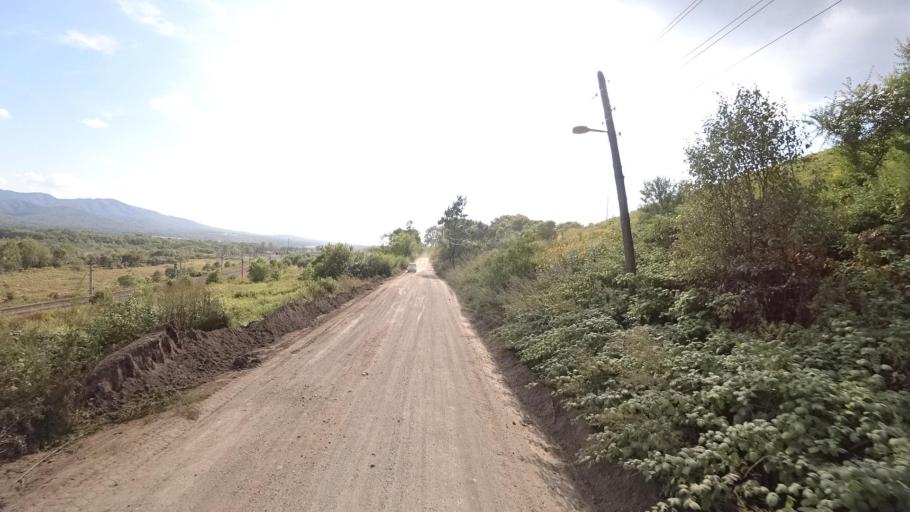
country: RU
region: Jewish Autonomous Oblast
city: Birakan
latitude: 49.0002
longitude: 131.7290
